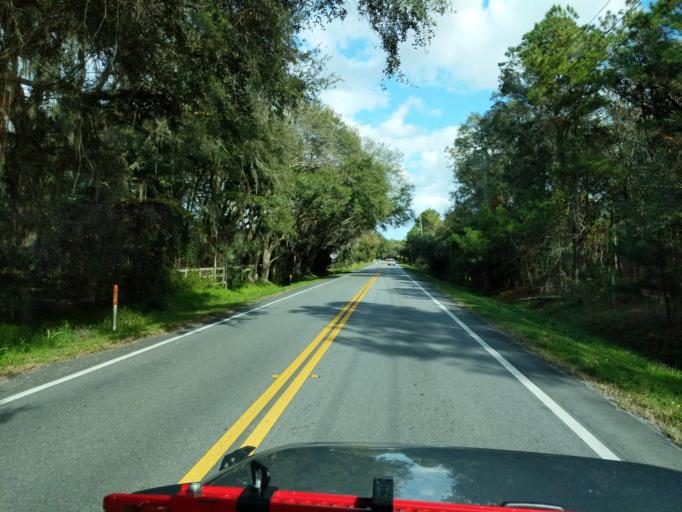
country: US
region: Florida
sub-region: Seminole County
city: Geneva
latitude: 28.6951
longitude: -81.1424
